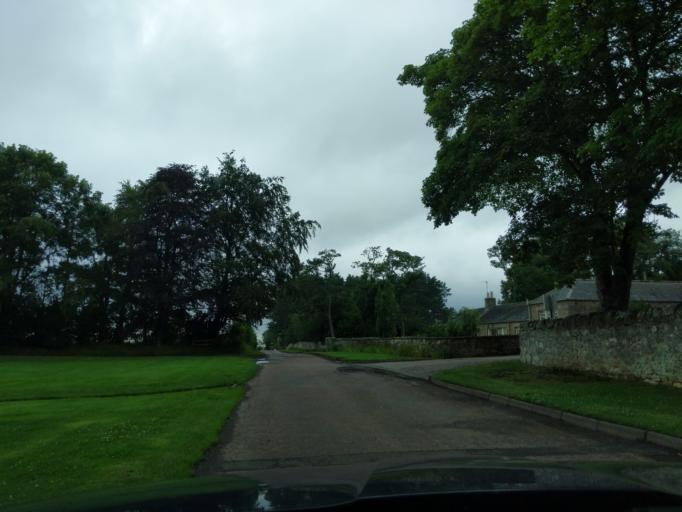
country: GB
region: England
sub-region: Northumberland
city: Ford
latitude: 55.6770
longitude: -2.1023
